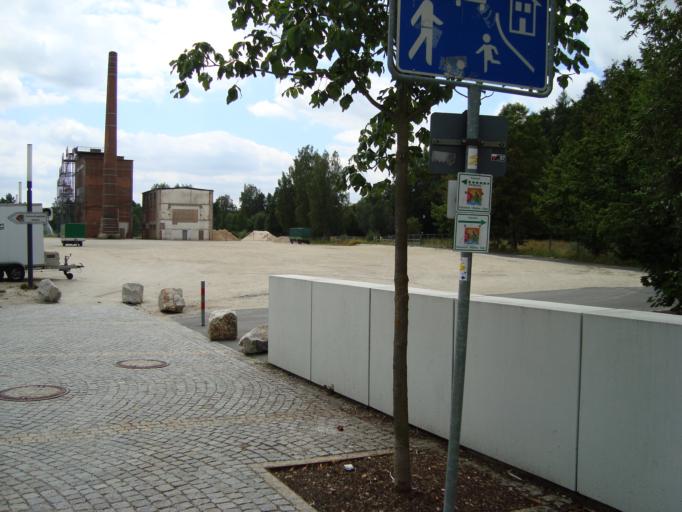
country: DE
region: Bavaria
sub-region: Upper Franconia
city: Marktredwitz
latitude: 49.9980
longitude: 12.0860
